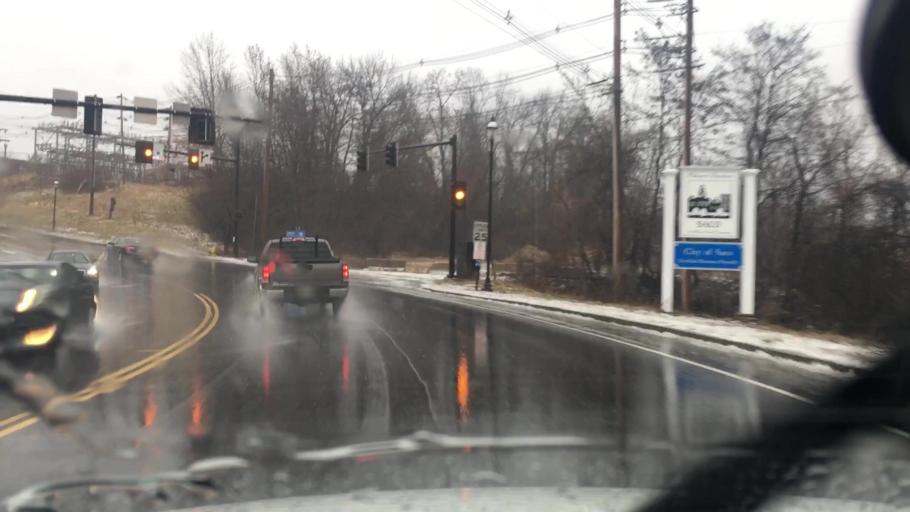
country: US
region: Maine
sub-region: York County
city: Biddeford
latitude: 43.4936
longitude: -70.4481
